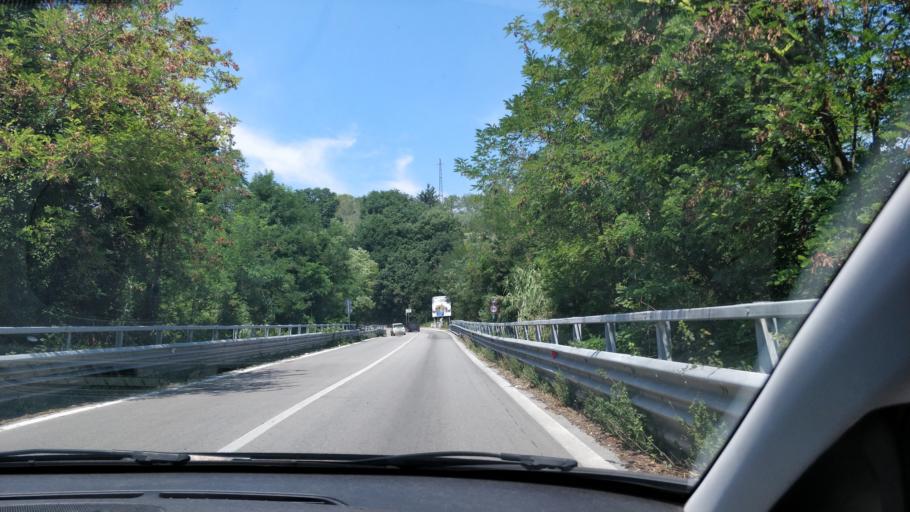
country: IT
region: Abruzzo
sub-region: Provincia di Chieti
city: Ortona
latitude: 42.3443
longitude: 14.4094
